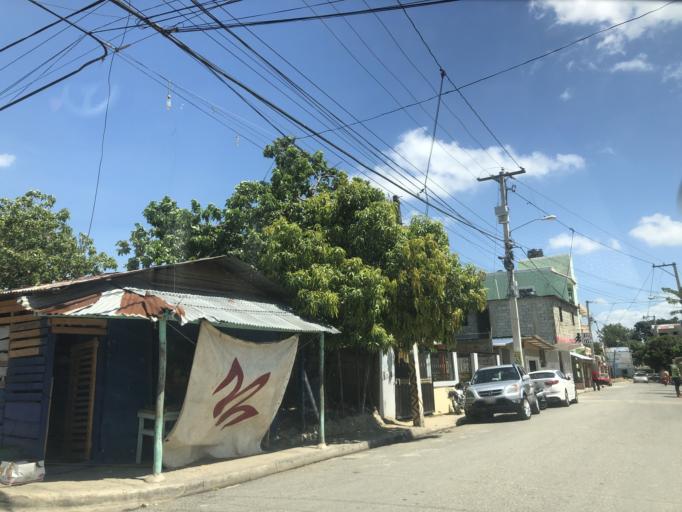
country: DO
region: Santiago
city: La Canela
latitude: 19.4517
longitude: -70.7819
